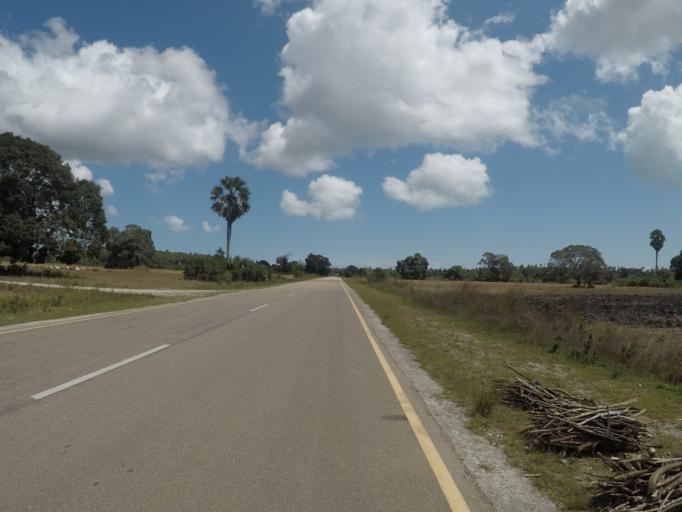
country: TZ
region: Zanzibar Central/South
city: Koani
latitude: -6.2254
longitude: 39.3612
